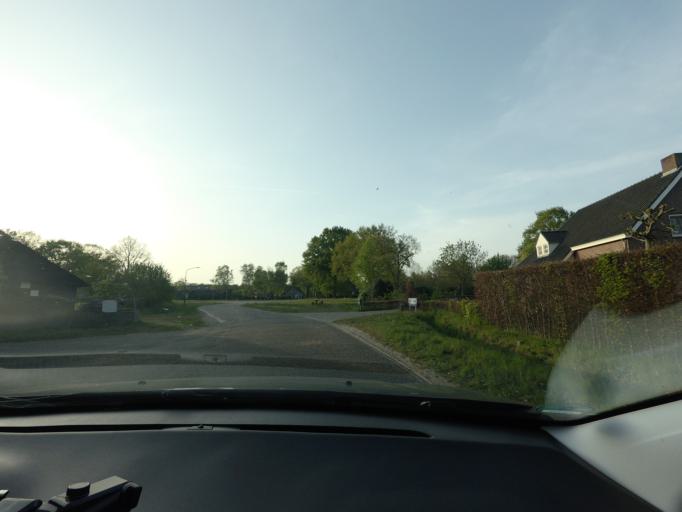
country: NL
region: North Brabant
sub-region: Gemeente Baarle-Nassau
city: Baarle-Nassau
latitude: 51.5036
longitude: 4.9737
